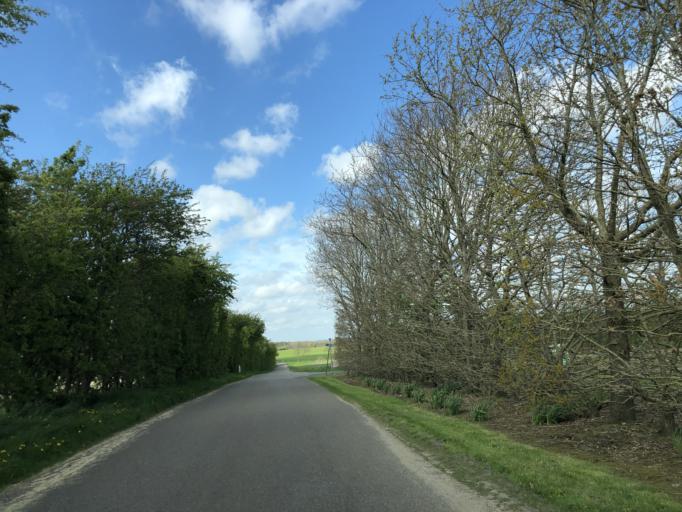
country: DK
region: Central Jutland
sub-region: Herning Kommune
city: Avlum
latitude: 56.3069
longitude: 8.7519
